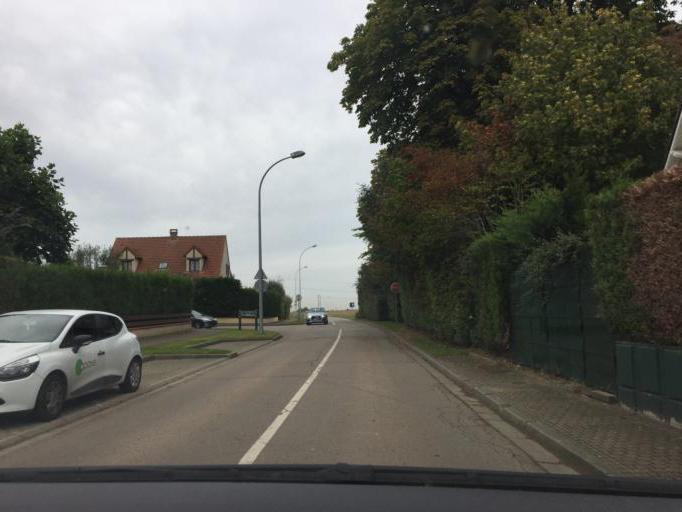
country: FR
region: Ile-de-France
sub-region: Departement de l'Essonne
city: Villiers-le-Bacle
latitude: 48.7271
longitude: 2.1264
